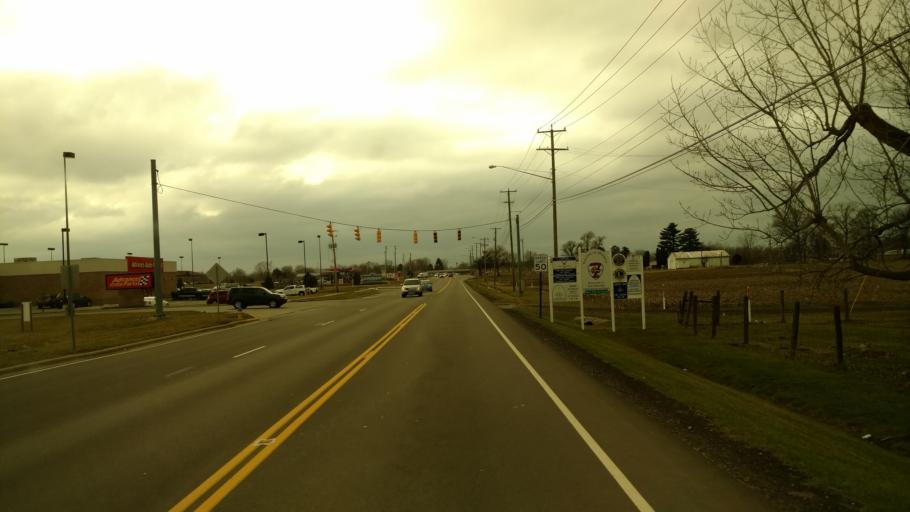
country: US
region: Ohio
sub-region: Licking County
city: Hebron
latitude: 39.9614
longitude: -82.4734
